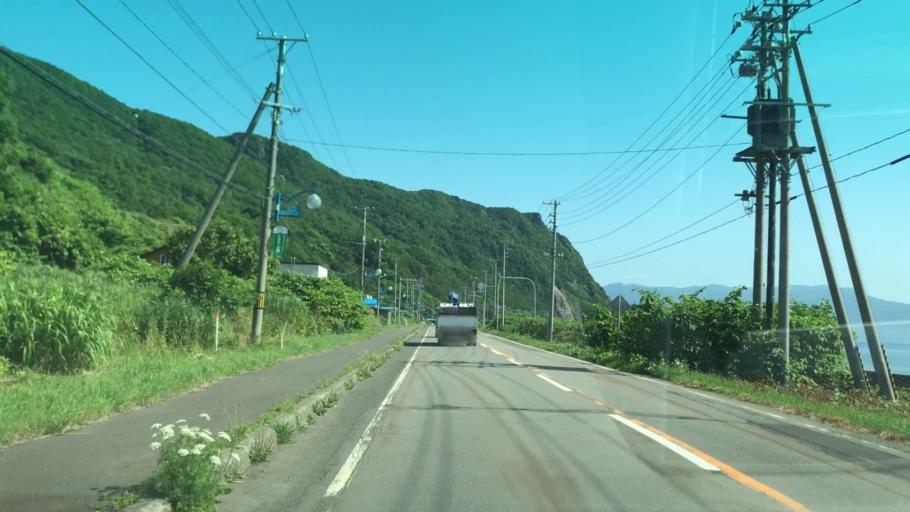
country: JP
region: Hokkaido
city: Iwanai
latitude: 43.0986
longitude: 140.4611
